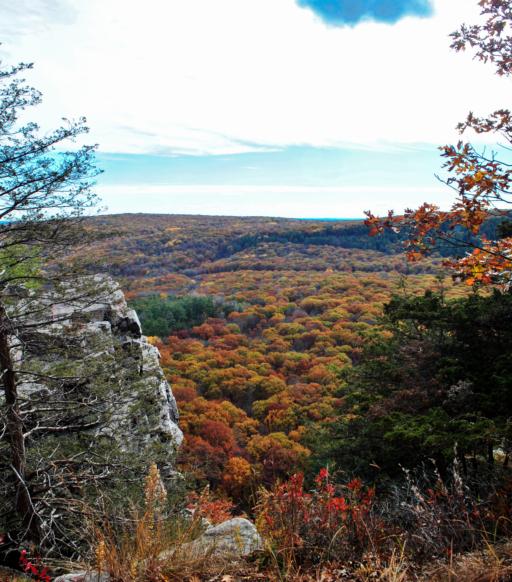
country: US
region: Wisconsin
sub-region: Sauk County
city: Baraboo
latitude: 43.4137
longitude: -89.7145
